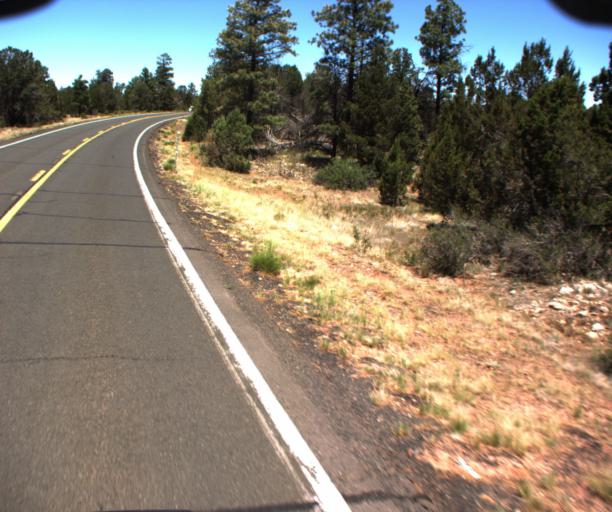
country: US
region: Arizona
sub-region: Gila County
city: Star Valley
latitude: 34.7000
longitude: -111.1053
